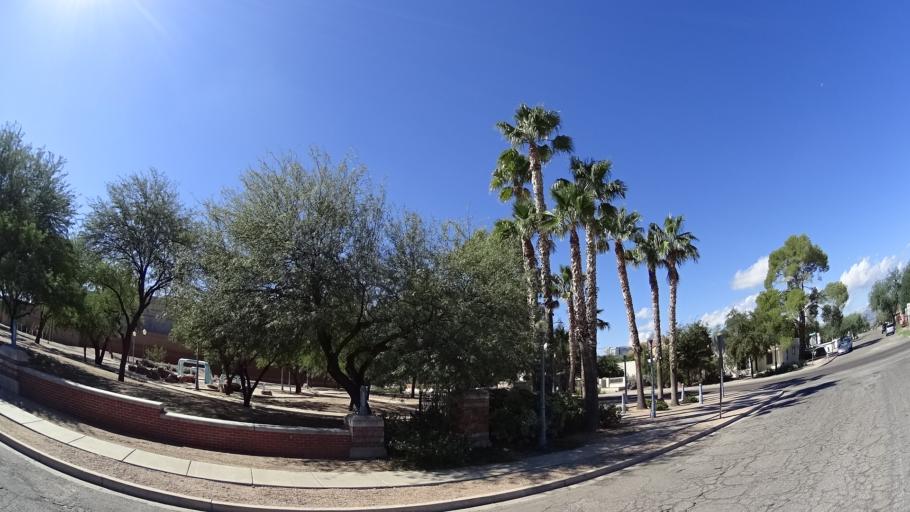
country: US
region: Arizona
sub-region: Pima County
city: Tucson
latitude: 32.2386
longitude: -110.9521
